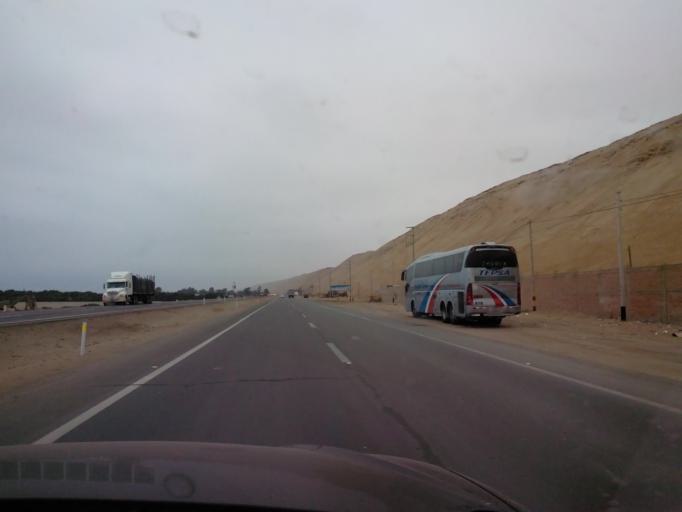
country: PE
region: Ica
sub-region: Provincia de Chincha
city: San Pedro
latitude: -13.3812
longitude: -76.2051
